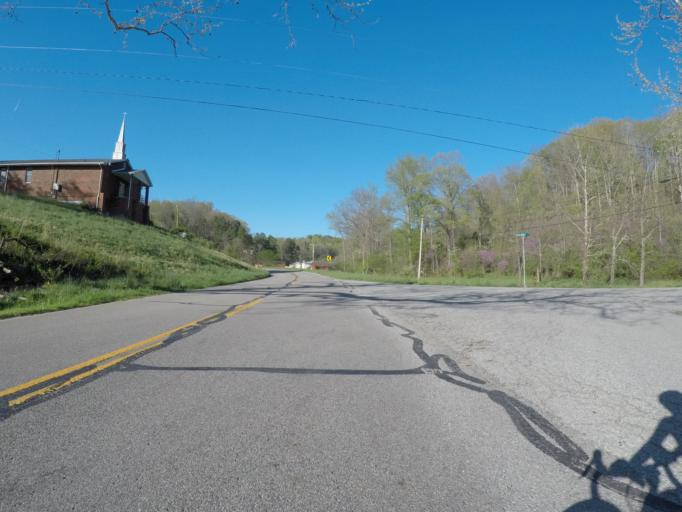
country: US
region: Kentucky
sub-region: Boyd County
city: Meads
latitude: 38.3666
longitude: -82.6647
